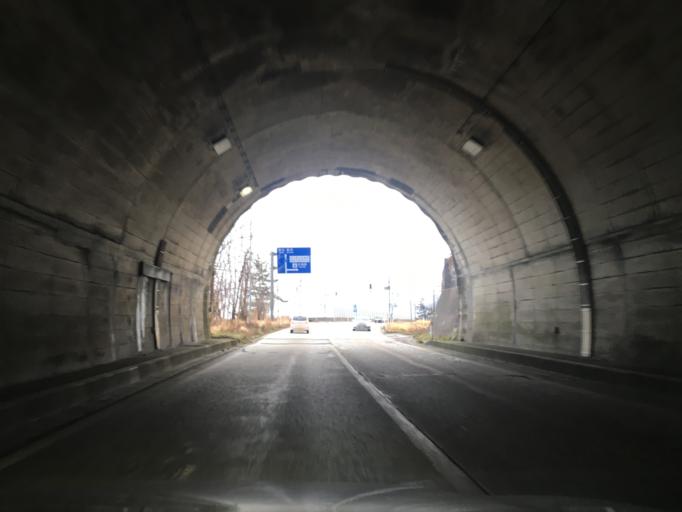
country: JP
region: Niigata
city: Murakami
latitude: 38.5080
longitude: 139.5257
